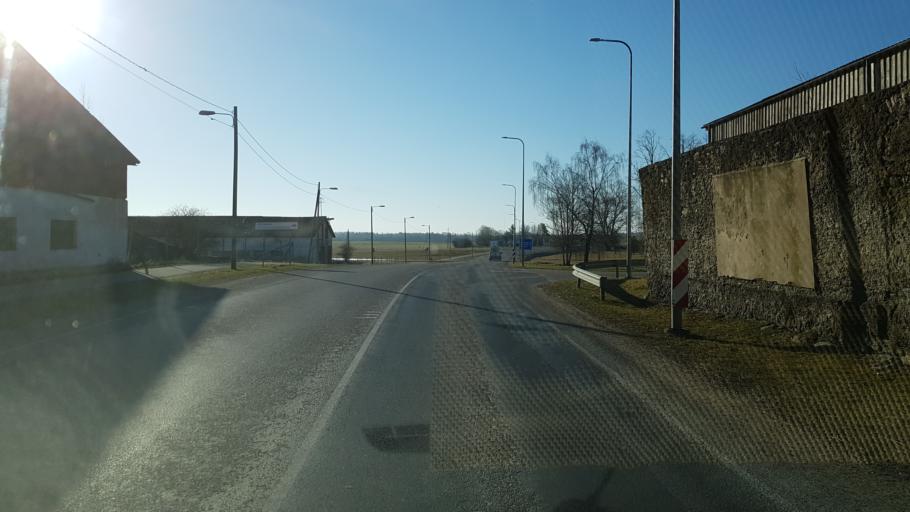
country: EE
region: Jaervamaa
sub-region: Tueri vald
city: Sarevere
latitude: 58.7845
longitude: 25.4315
